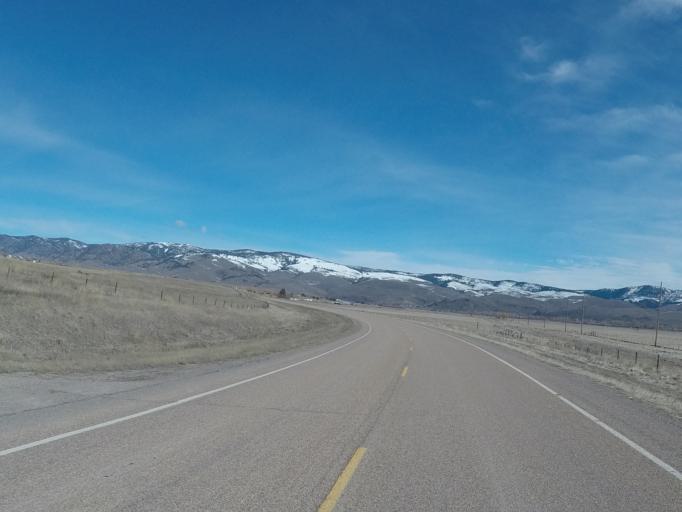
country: US
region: Montana
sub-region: Granite County
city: Philipsburg
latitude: 46.6239
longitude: -113.1709
